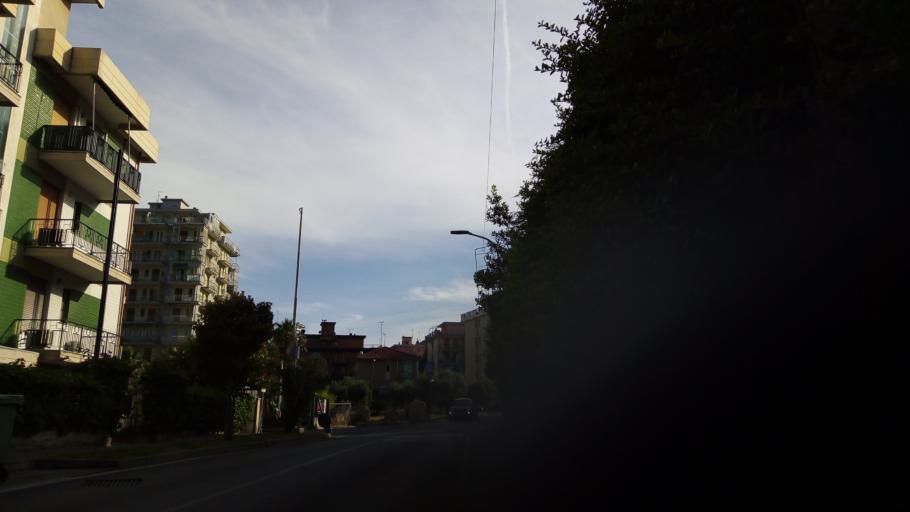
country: IT
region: Liguria
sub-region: Provincia di Savona
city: Borghetto Santo Spirito
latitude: 44.1187
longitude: 8.2478
